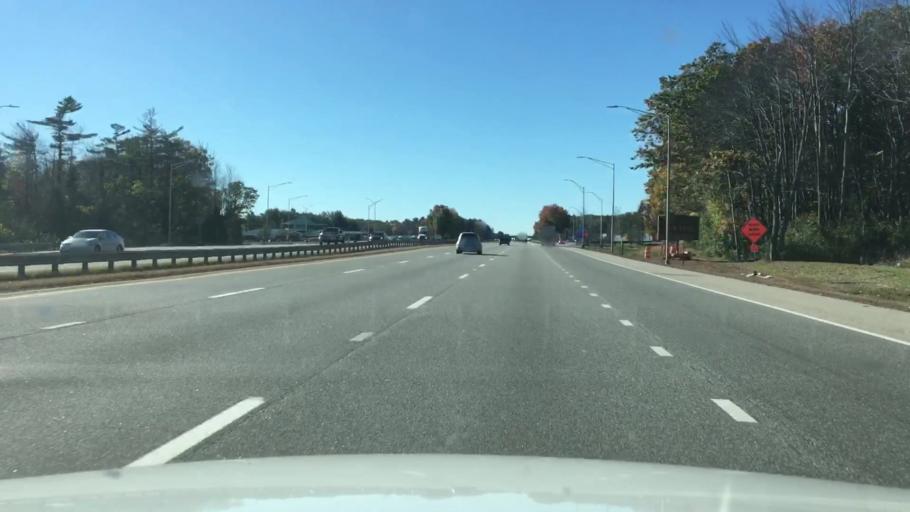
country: US
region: Maine
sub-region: York County
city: West Kennebunk
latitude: 43.4145
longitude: -70.5575
